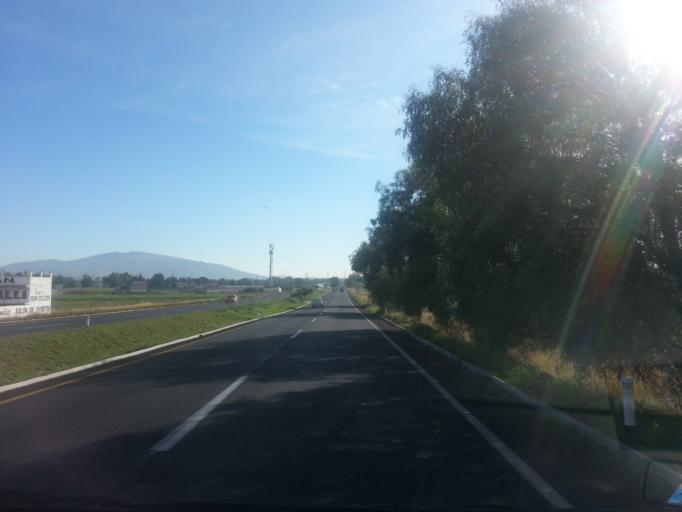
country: MX
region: Morelos
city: Xometla
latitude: 19.6436
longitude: -98.8941
